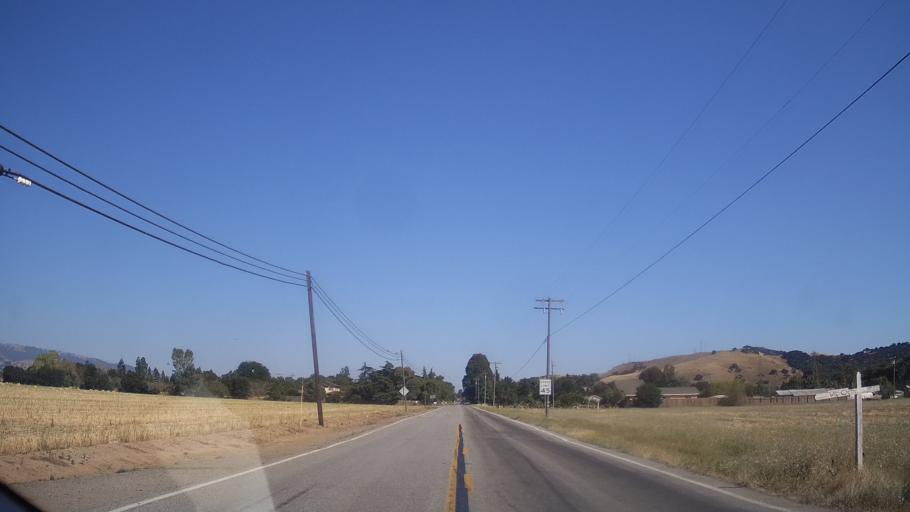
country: US
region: California
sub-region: Santa Clara County
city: Morgan Hill
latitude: 37.1654
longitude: -121.6916
